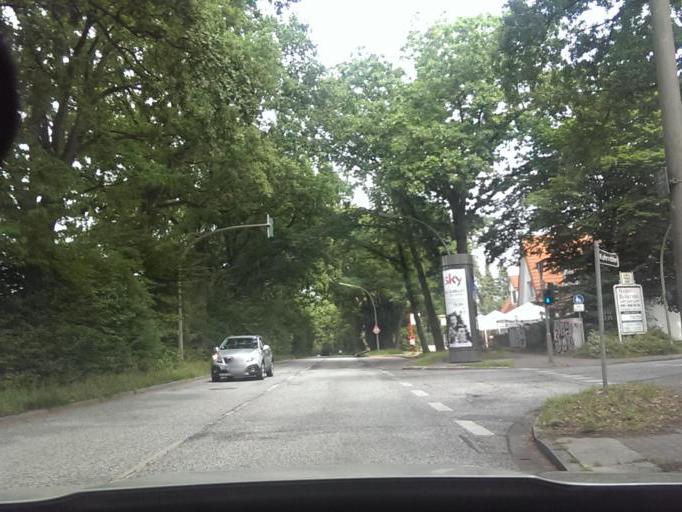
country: DE
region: Hamburg
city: Lemsahl-Mellingstedt
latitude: 53.6752
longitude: 10.0928
